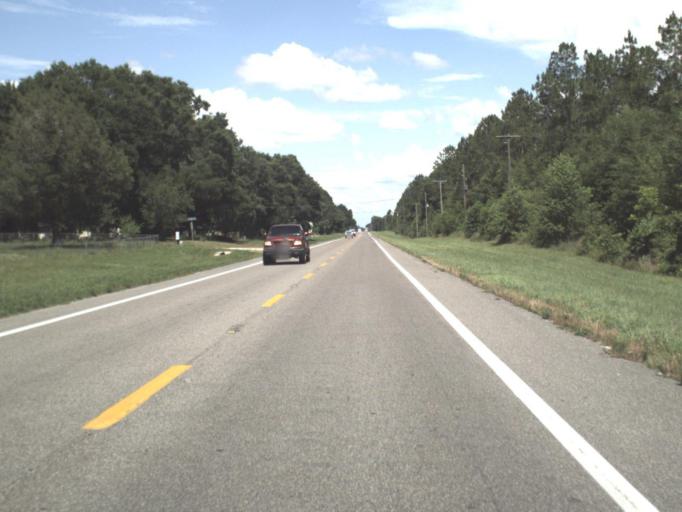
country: US
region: Florida
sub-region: Lafayette County
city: Mayo
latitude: 30.0529
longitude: -83.1417
